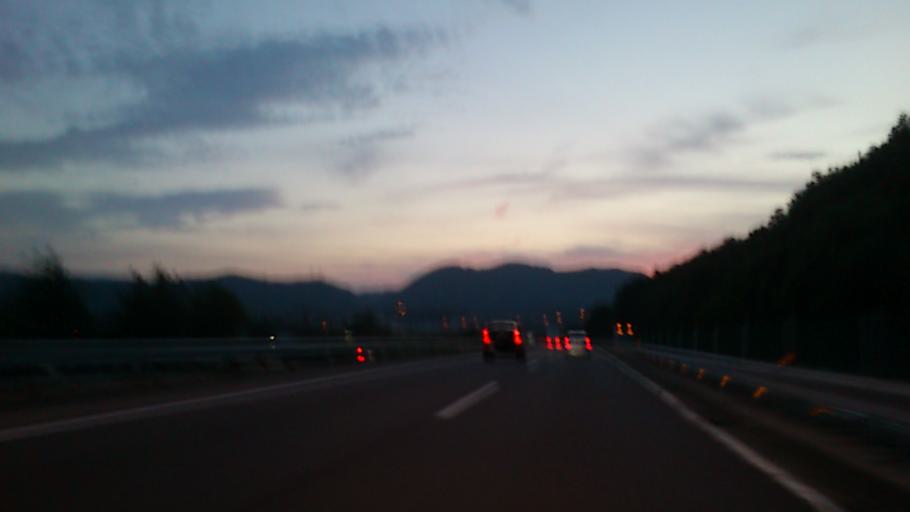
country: JP
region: Gifu
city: Tajimi
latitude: 35.3484
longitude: 137.1124
